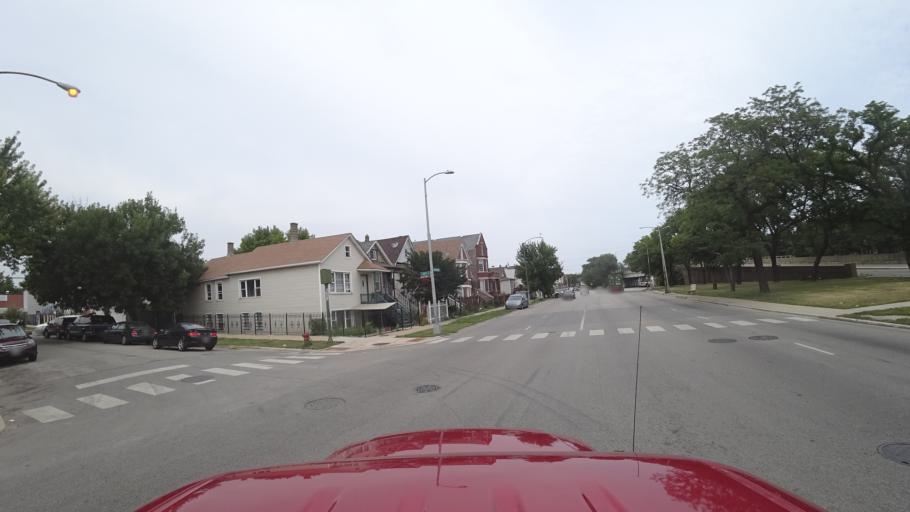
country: US
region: Illinois
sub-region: Cook County
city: Chicago
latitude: 41.8320
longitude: -87.6850
